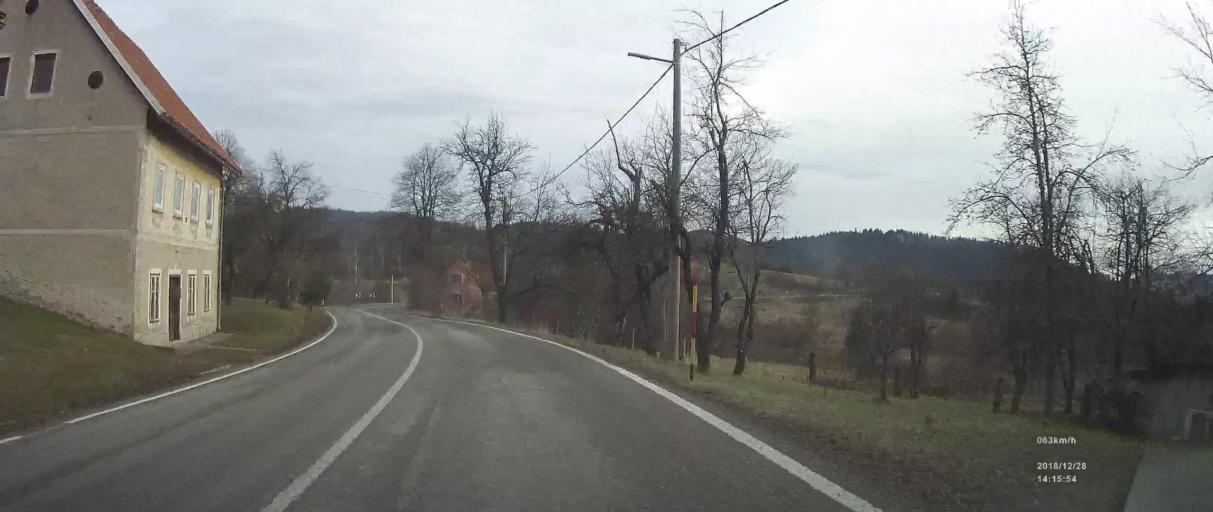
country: HR
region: Primorsko-Goranska
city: Vrbovsko
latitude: 45.4218
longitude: 15.0311
